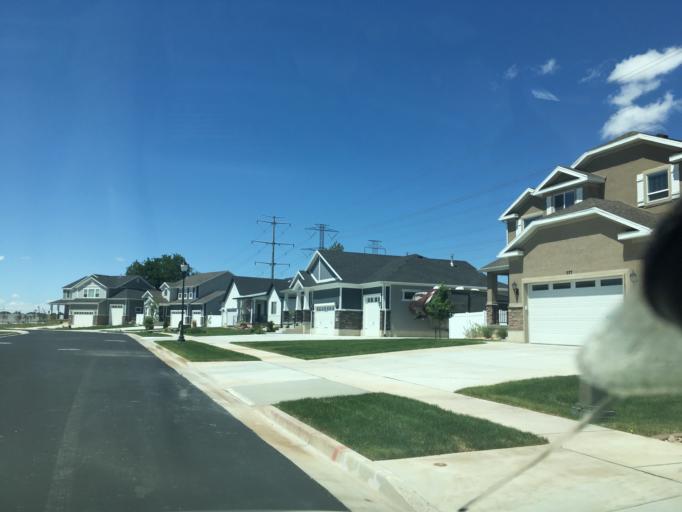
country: US
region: Utah
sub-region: Davis County
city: Layton
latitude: 41.0519
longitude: -112.0040
